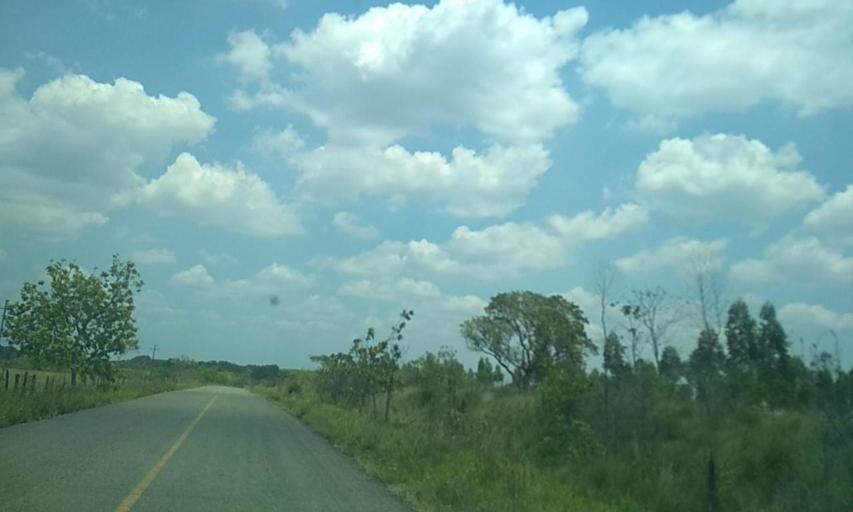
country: MX
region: Tabasco
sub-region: Huimanguillo
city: Francisco Rueda
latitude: 17.7917
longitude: -93.8426
